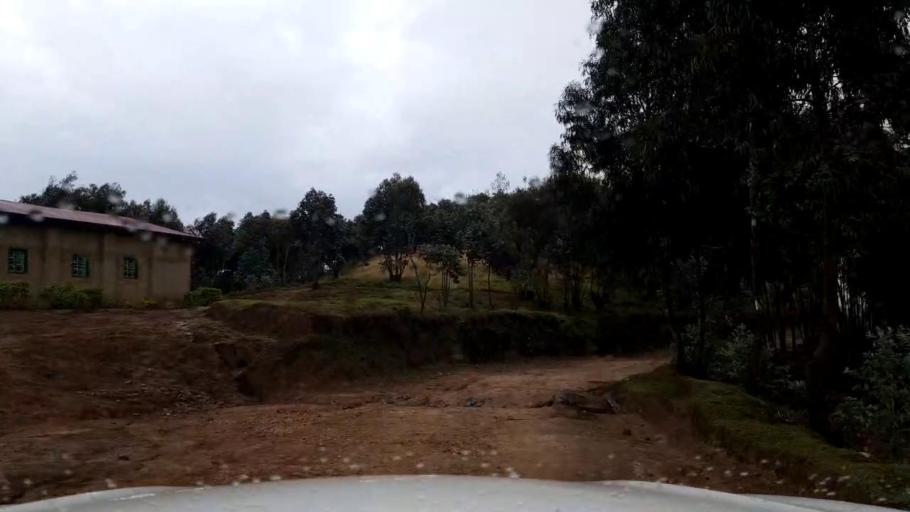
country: RW
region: Western Province
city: Kibuye
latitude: -2.0153
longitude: 29.4703
